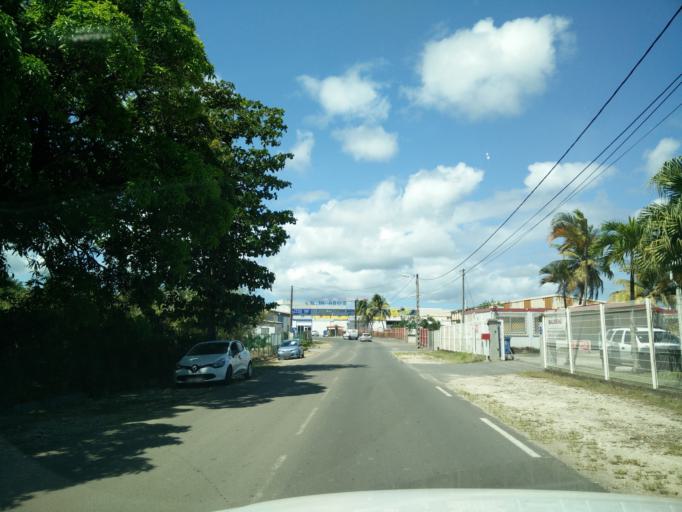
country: GP
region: Guadeloupe
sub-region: Guadeloupe
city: Pointe-a-Pitre
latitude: 16.2391
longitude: -61.5643
